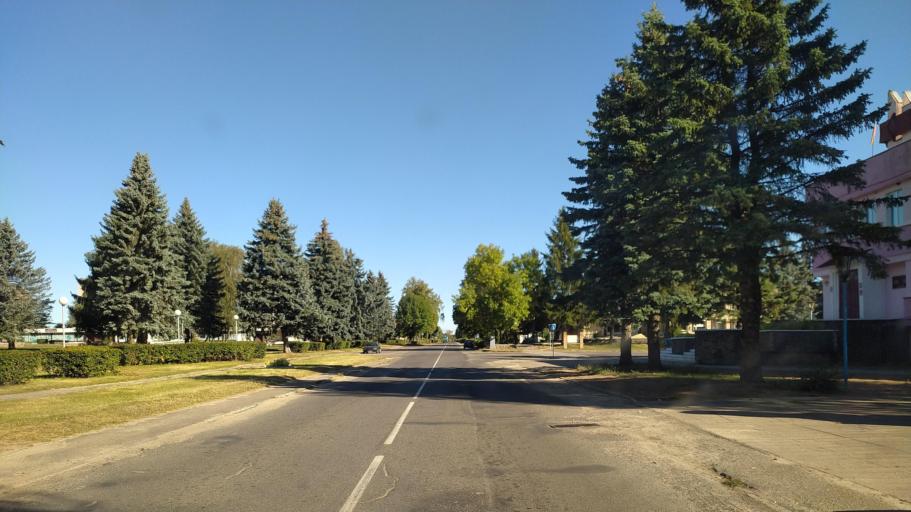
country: BY
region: Brest
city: Pruzhany
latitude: 52.4870
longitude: 24.7076
